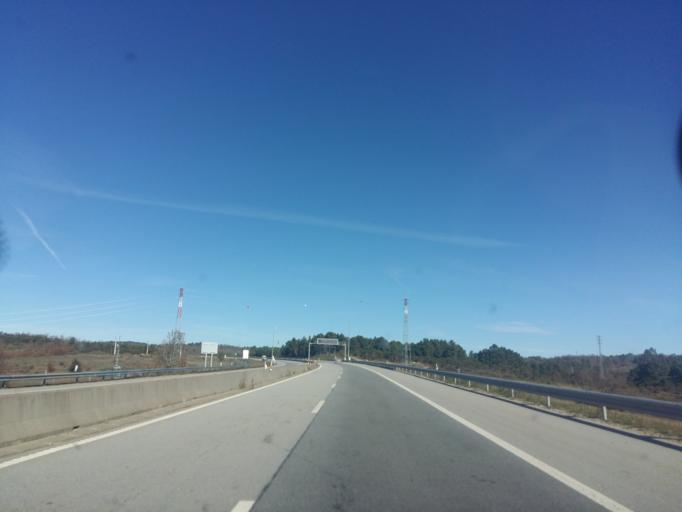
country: PT
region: Guarda
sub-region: Guarda
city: Sequeira
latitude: 40.5290
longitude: -7.2200
